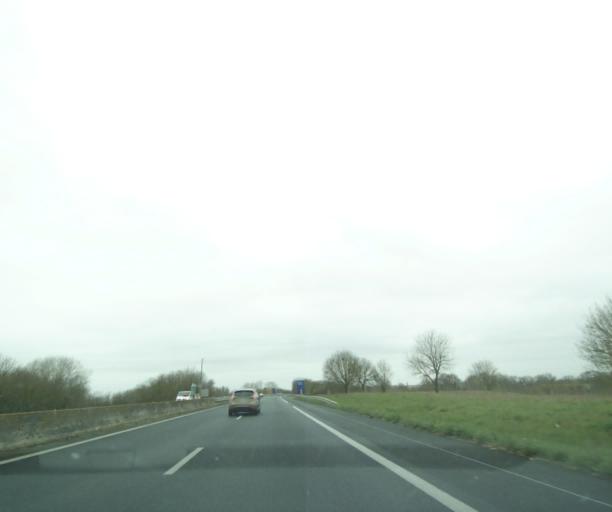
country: FR
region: Poitou-Charentes
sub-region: Departement de la Charente-Maritime
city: Breuil-Magne
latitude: 45.9666
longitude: -0.9761
